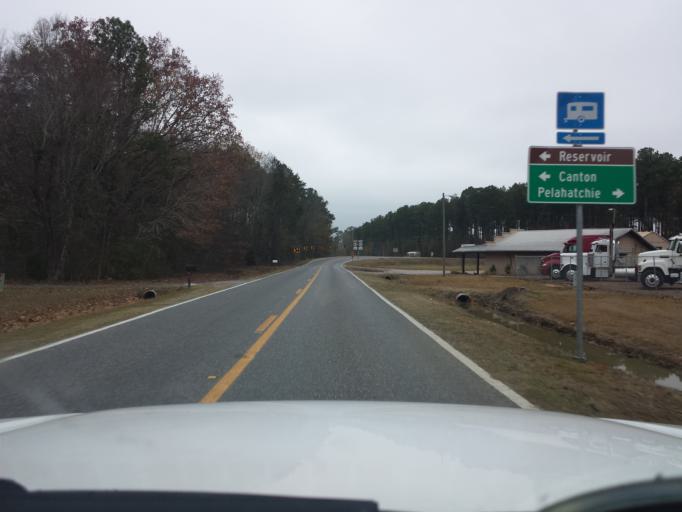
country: US
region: Mississippi
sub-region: Madison County
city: Canton
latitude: 32.4977
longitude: -89.9253
